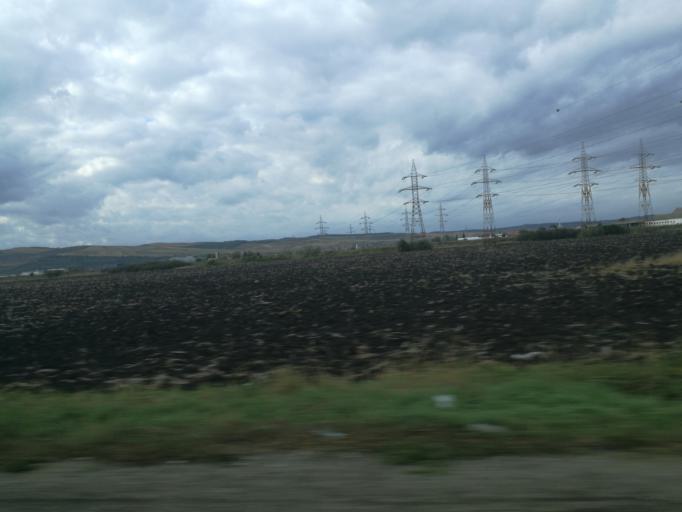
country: RO
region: Mures
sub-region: Comuna Cristesti
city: Cristesti
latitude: 46.4959
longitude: 24.4788
